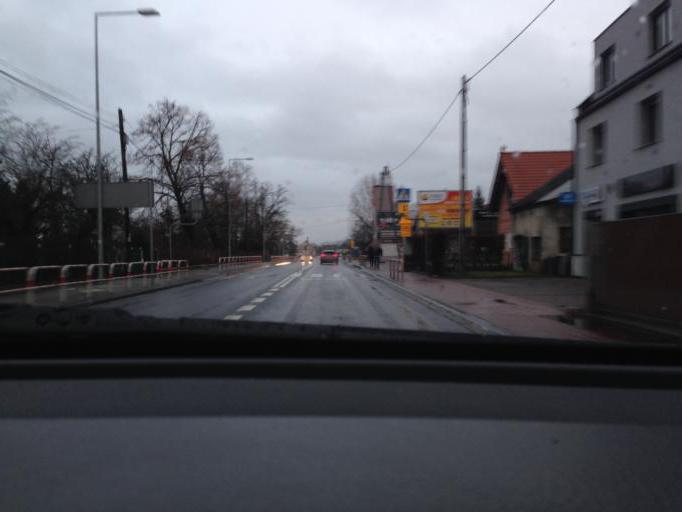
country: PL
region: Opole Voivodeship
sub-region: Powiat opolski
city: Wegry
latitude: 50.7131
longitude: 17.9925
